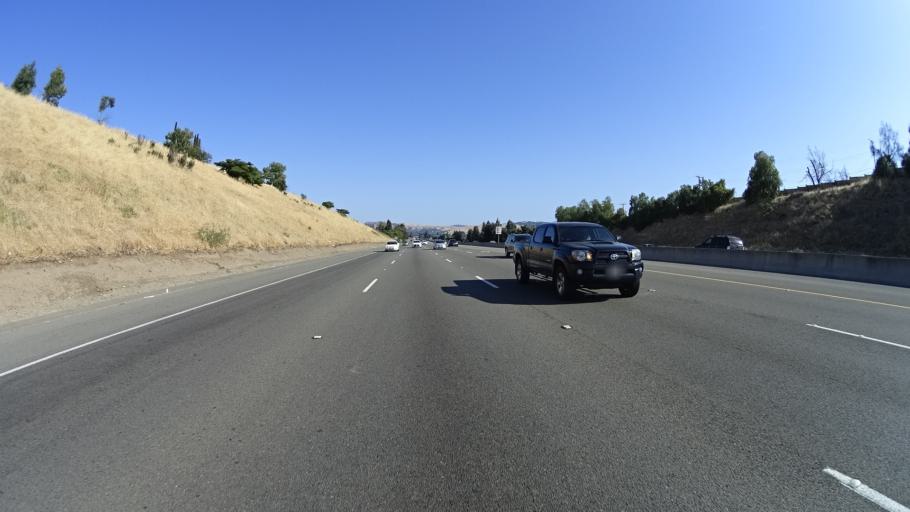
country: US
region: California
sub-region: Santa Clara County
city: Seven Trees
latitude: 37.2736
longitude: -121.8040
